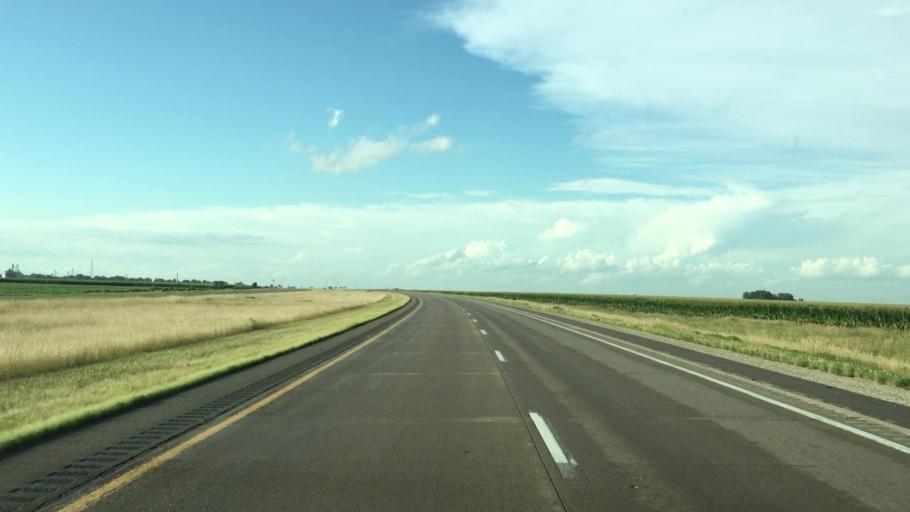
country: US
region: Iowa
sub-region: Henry County
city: Winfield
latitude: 41.1093
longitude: -91.5402
